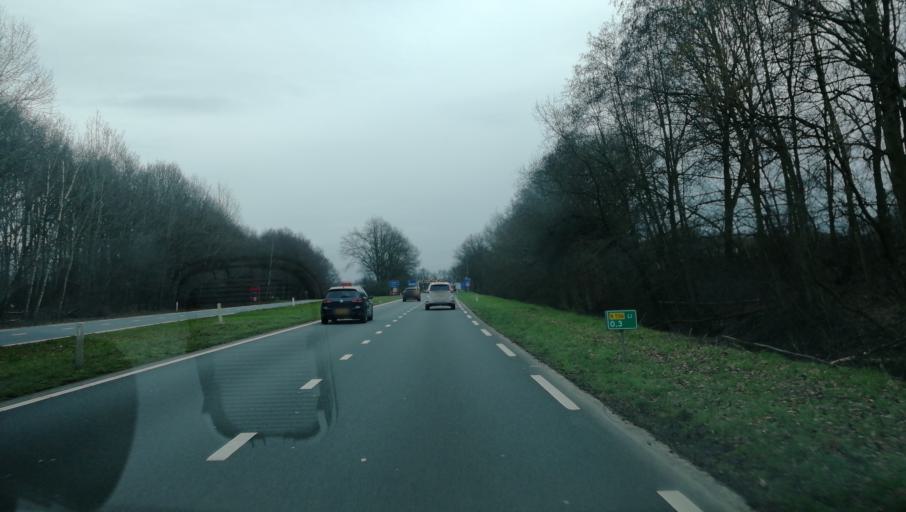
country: NL
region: Limburg
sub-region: Gemeente Venlo
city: Venlo
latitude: 51.3817
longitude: 6.1332
